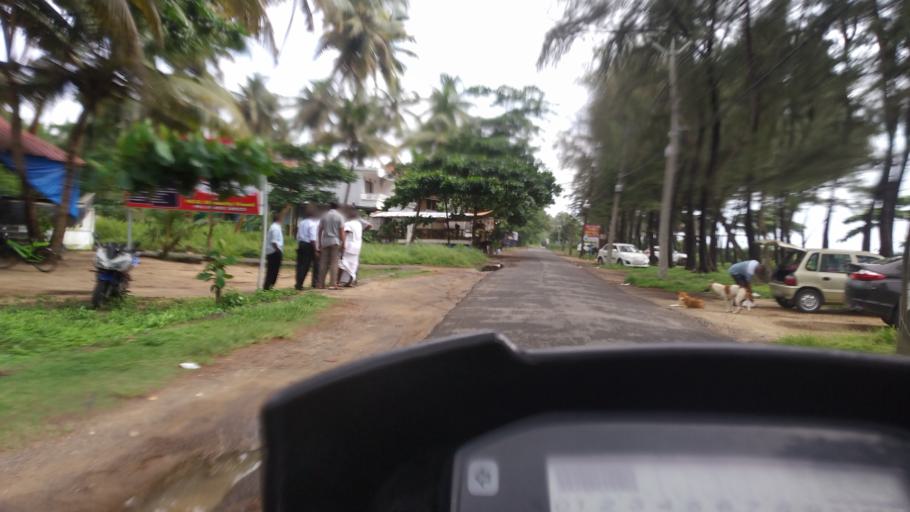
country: IN
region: Kerala
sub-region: Thrissur District
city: Kodungallur
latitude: 10.1524
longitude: 76.1749
